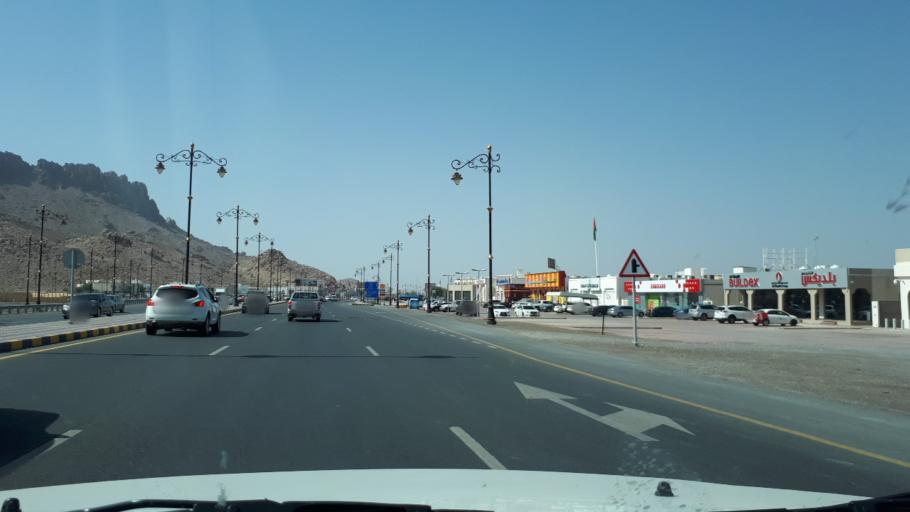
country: OM
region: Muhafazat ad Dakhiliyah
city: Nizwa
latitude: 22.9096
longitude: 57.5344
